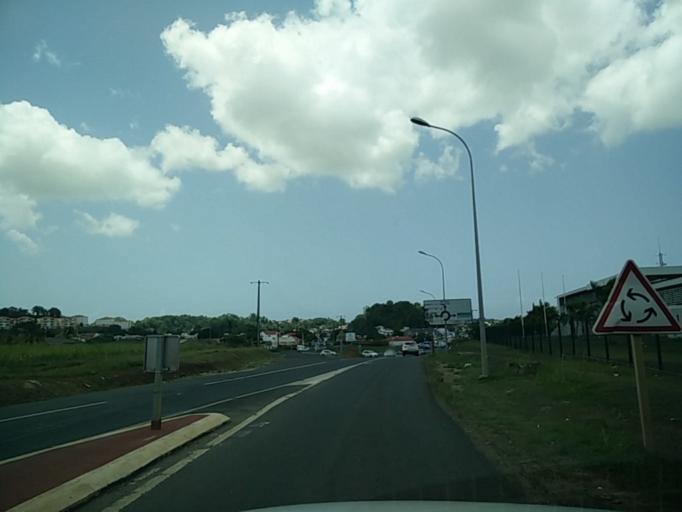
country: GP
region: Guadeloupe
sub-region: Guadeloupe
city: Les Abymes
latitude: 16.2785
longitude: -61.5096
